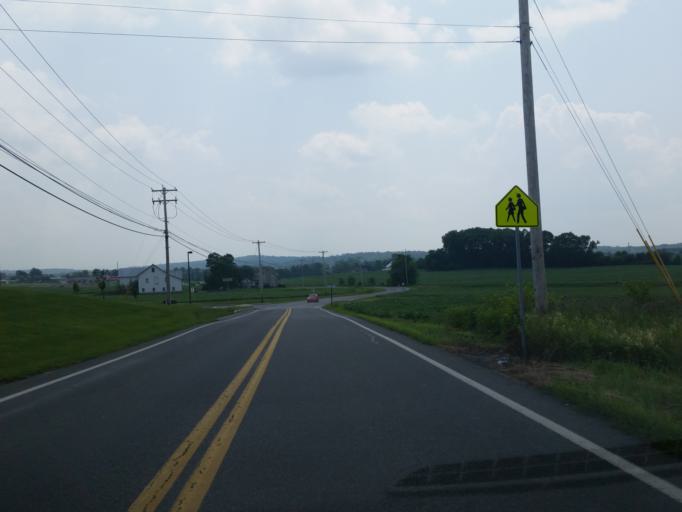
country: US
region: Pennsylvania
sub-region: Lebanon County
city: Campbelltown
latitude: 40.2888
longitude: -76.5987
